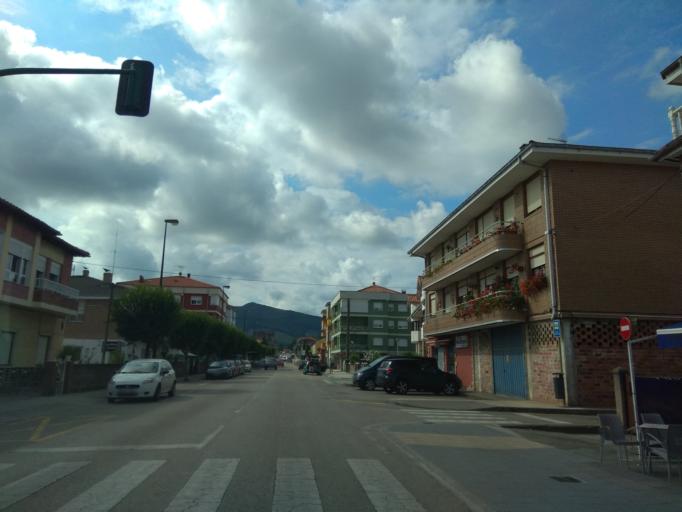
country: ES
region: Cantabria
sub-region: Provincia de Cantabria
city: Torrelavega
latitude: 43.3399
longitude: -4.0460
